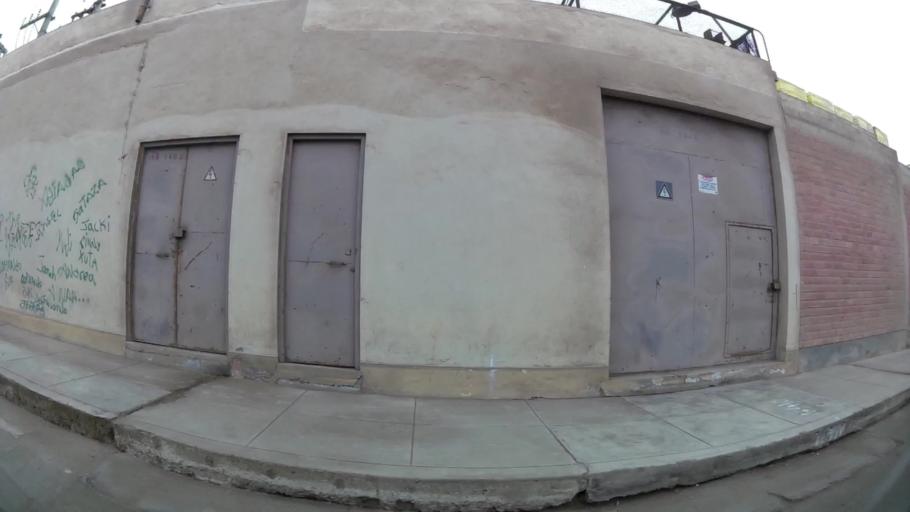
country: PE
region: Lima
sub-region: Lima
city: Punta Hermosa
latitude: -12.2921
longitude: -76.8350
